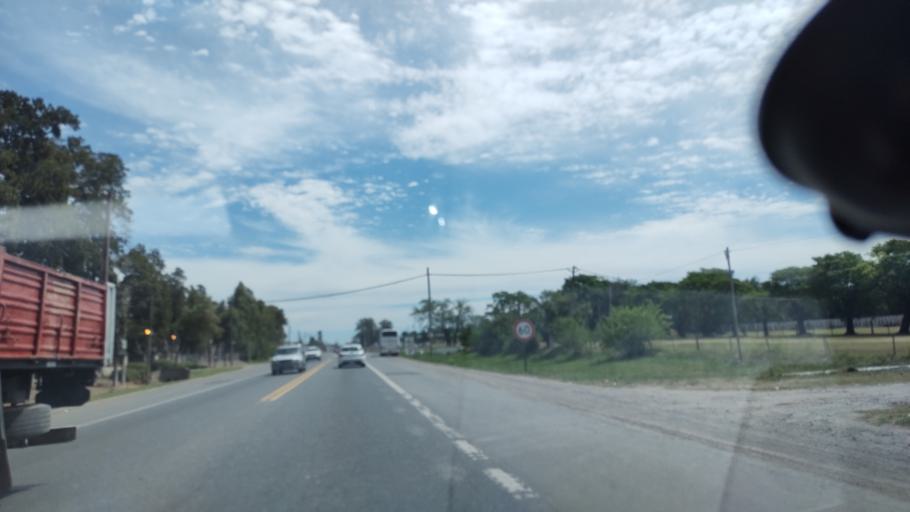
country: AR
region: Buenos Aires
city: Canuelas
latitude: -35.0380
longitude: -58.7587
